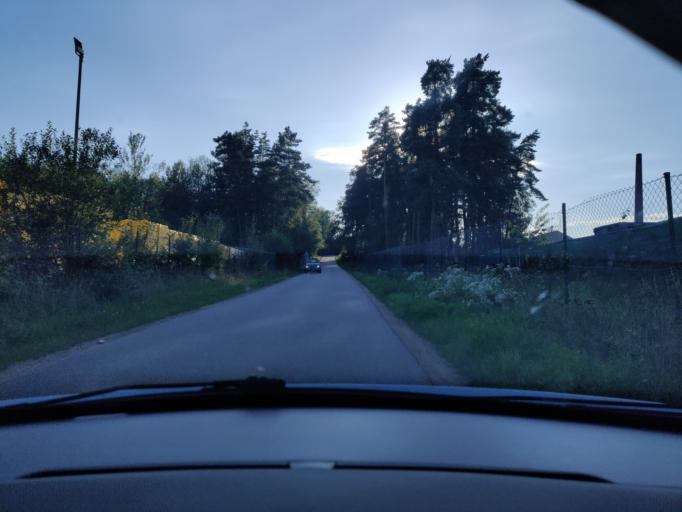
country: DE
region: Bavaria
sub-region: Upper Palatinate
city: Stulln
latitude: 49.4243
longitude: 12.1548
